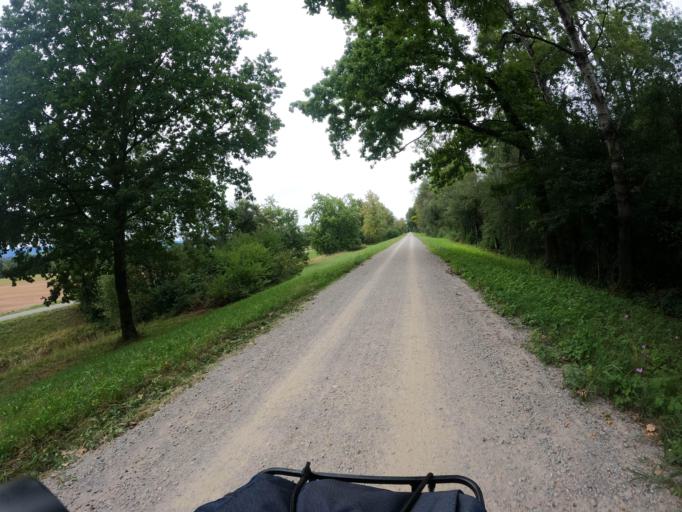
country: CH
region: Zurich
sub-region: Bezirk Affoltern
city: Ottenbach
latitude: 47.2729
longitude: 8.3985
